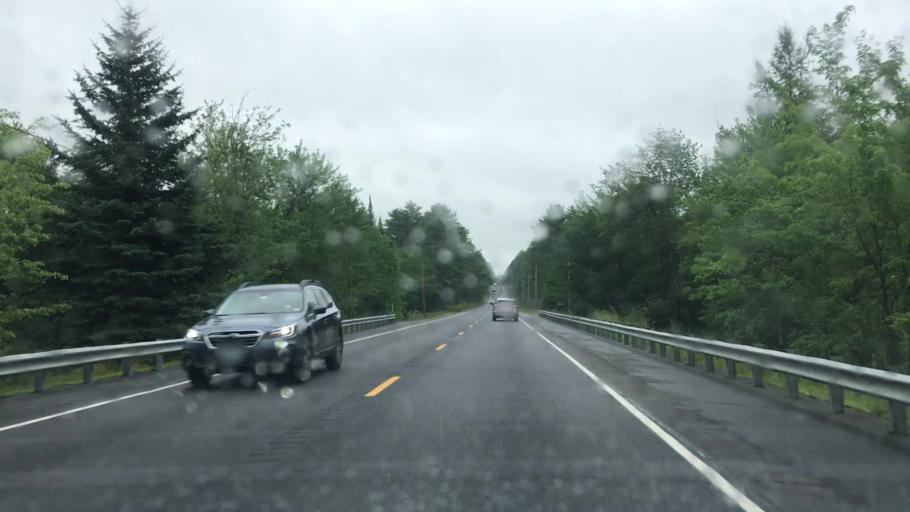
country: US
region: Maine
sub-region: Knox County
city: Washington
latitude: 44.2286
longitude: -69.3437
